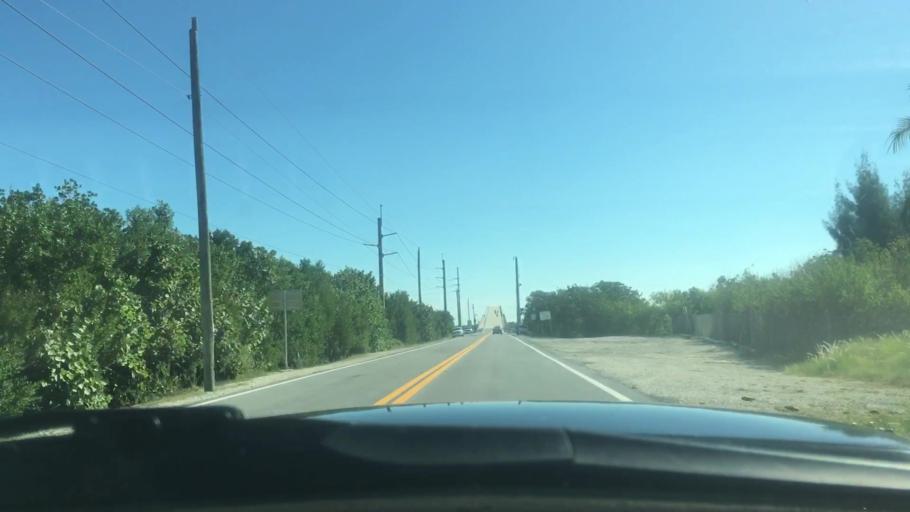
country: US
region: Florida
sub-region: Monroe County
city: North Key Largo
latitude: 25.2902
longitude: -80.3755
